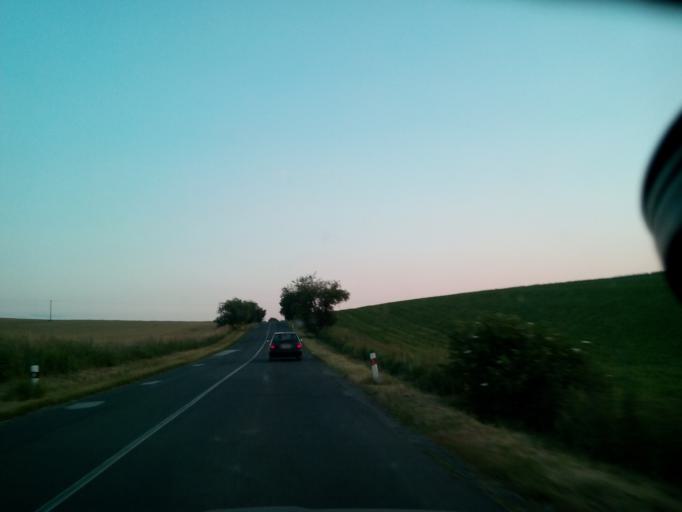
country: SK
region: Presovsky
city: Lubica
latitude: 49.0952
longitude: 20.4313
